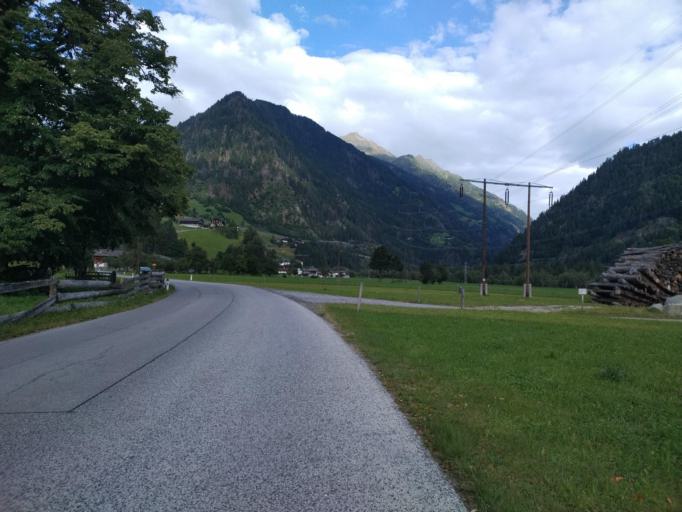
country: AT
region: Tyrol
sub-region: Politischer Bezirk Lienz
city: Hopfgarten in Defereggen
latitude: 46.9250
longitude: 12.5892
